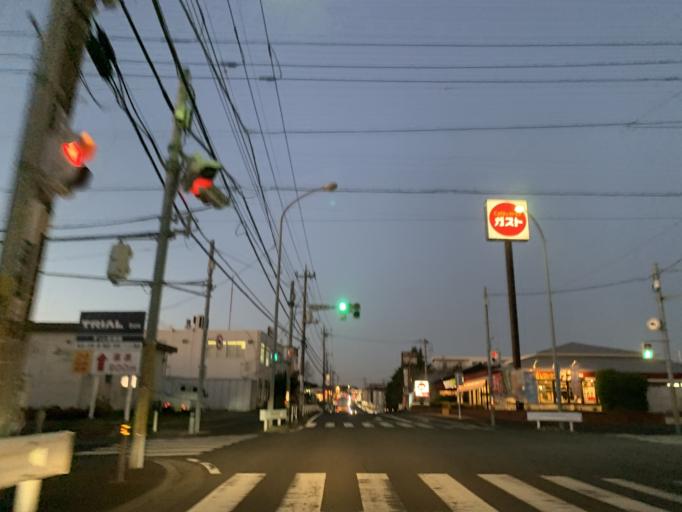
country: JP
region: Chiba
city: Nagareyama
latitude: 35.8915
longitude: 139.9008
